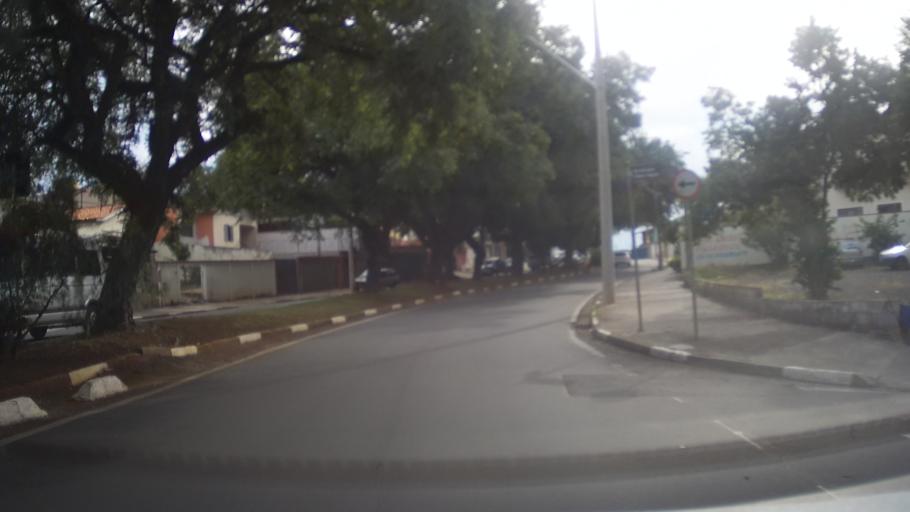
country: BR
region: Sao Paulo
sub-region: Campinas
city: Campinas
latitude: -22.9003
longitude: -47.1019
